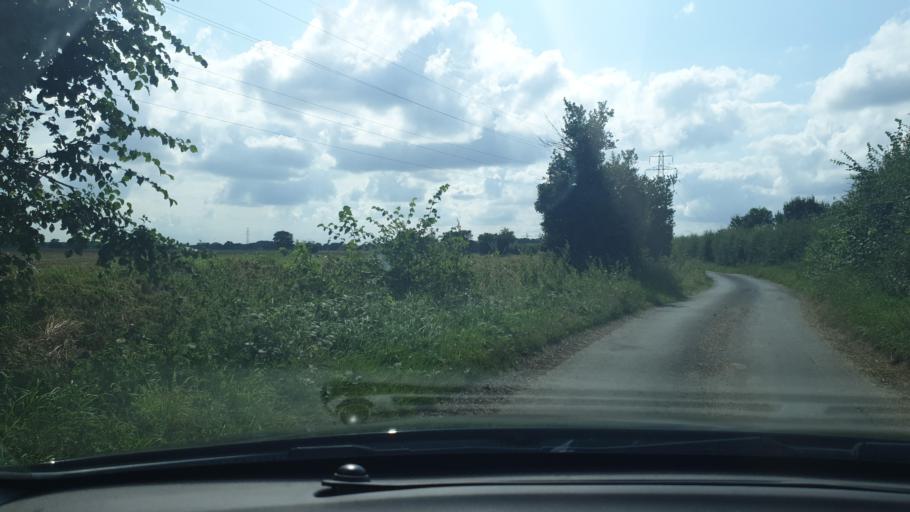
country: GB
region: England
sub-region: Essex
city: Manningtree
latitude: 51.9226
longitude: 1.0272
